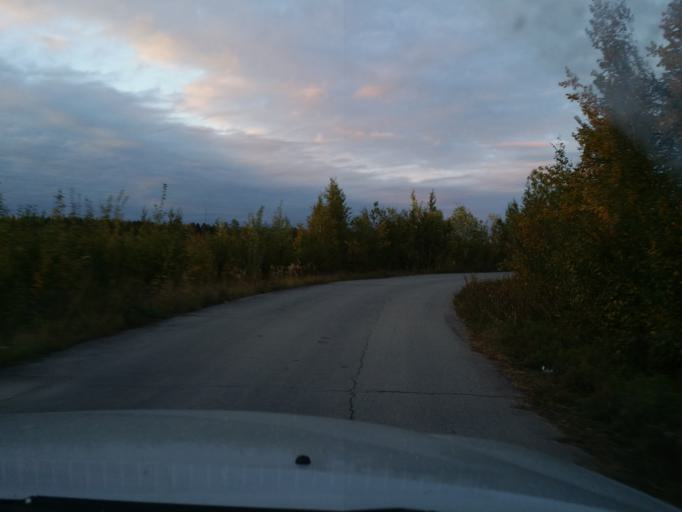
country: RU
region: Khanty-Mansiyskiy Avtonomnyy Okrug
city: Megion
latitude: 61.0830
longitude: 76.1606
